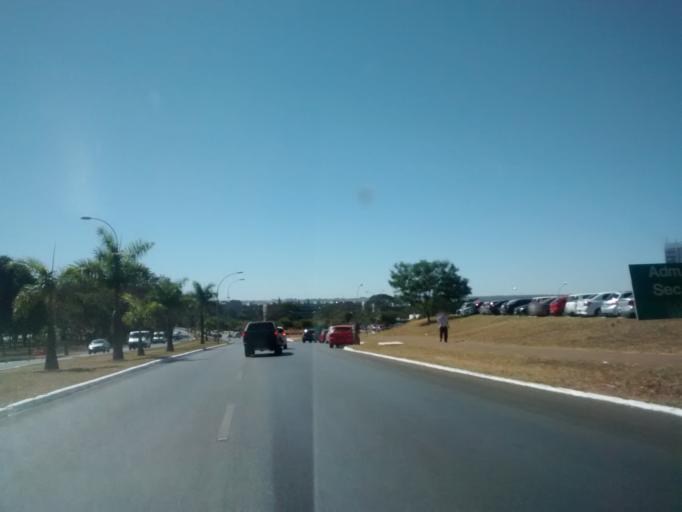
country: BR
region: Federal District
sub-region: Brasilia
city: Brasilia
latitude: -15.7876
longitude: -47.8803
